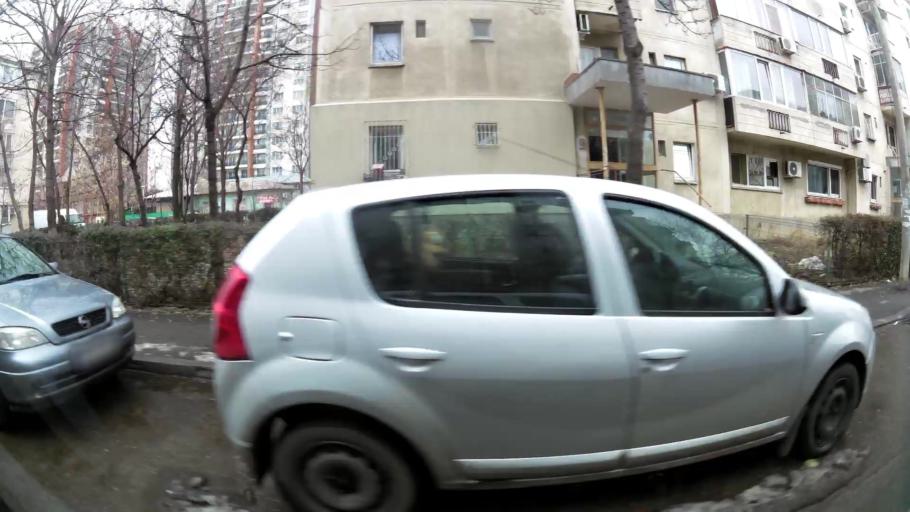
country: RO
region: Bucuresti
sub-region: Municipiul Bucuresti
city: Bucharest
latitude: 44.4186
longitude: 26.1332
